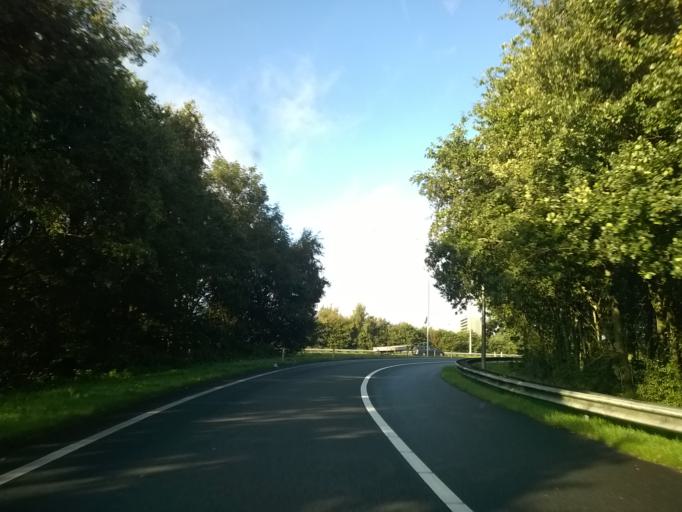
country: NL
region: Friesland
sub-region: Gemeente Smallingerland
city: Drachtstercompagnie
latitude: 53.1067
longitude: 6.1340
